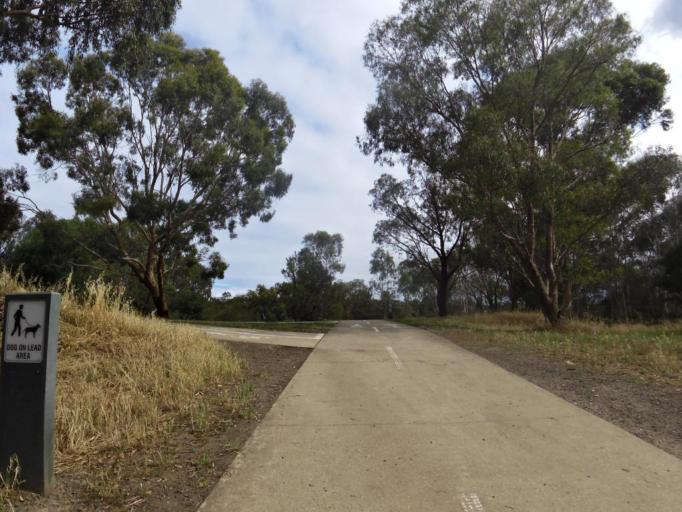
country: AU
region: Victoria
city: Alphington
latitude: -37.7747
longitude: 145.0345
